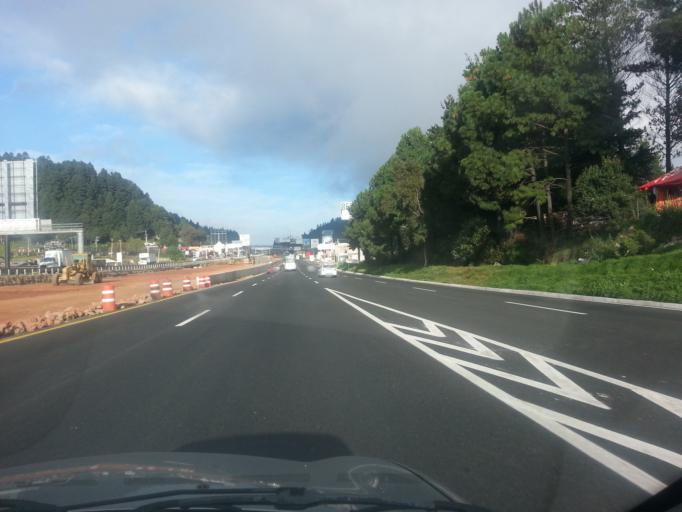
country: MX
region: Morelos
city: San Jeronimo Acazulco
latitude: 19.3008
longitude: -99.3796
